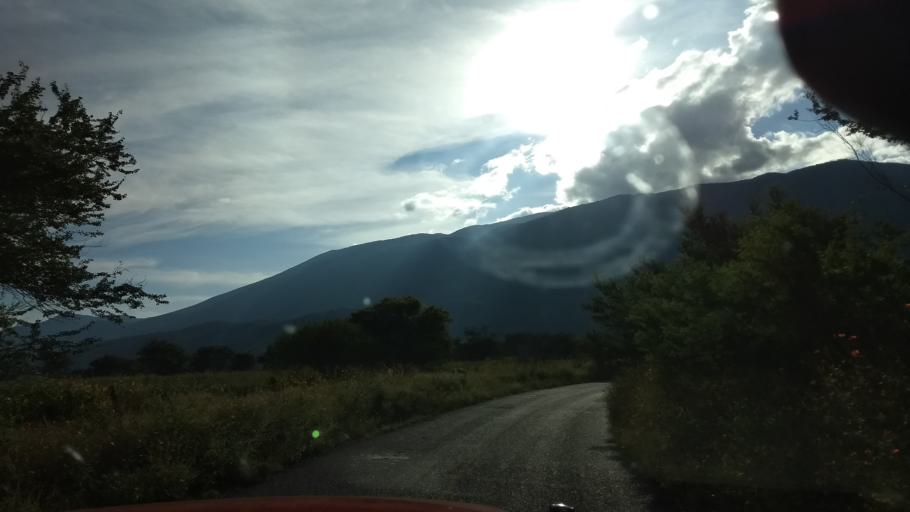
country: MX
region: Colima
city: Suchitlan
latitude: 19.4488
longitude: -103.8144
